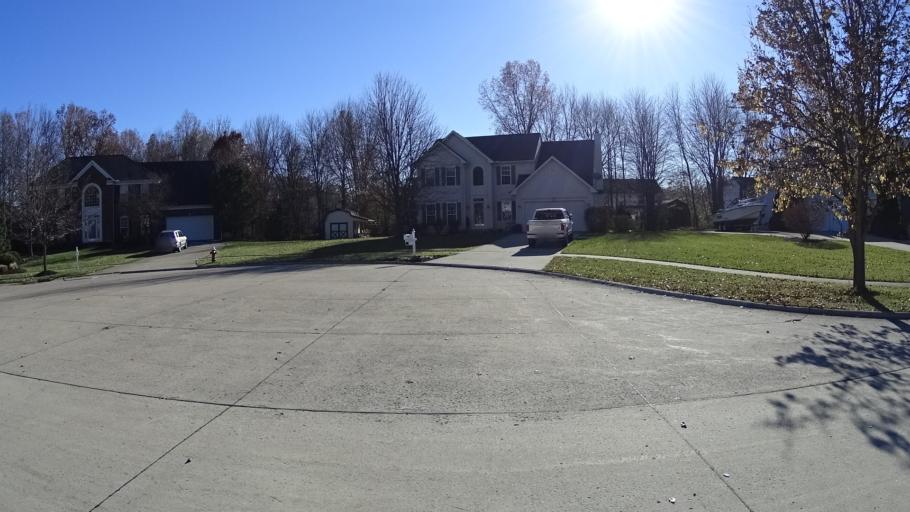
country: US
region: Ohio
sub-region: Lorain County
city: Avon Center
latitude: 41.4455
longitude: -81.9932
